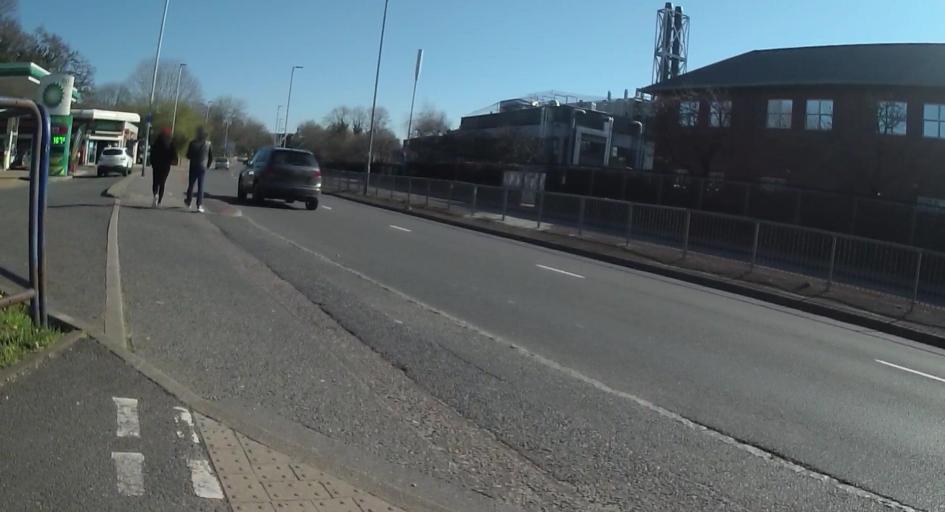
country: GB
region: England
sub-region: Bracknell Forest
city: Bracknell
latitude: 51.4152
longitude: -0.7340
